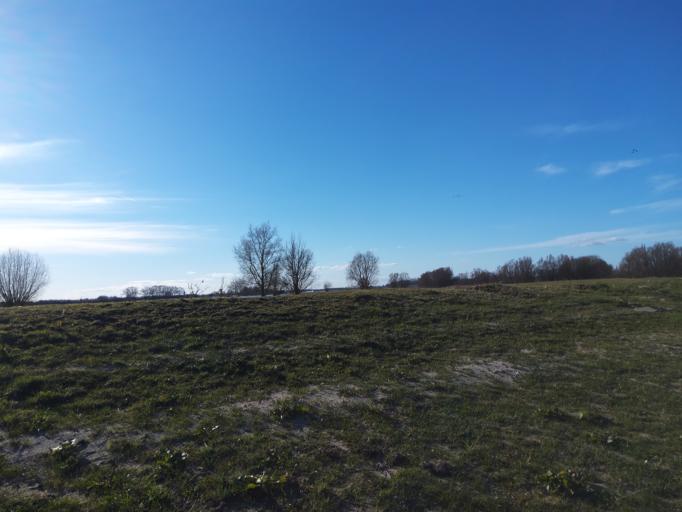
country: NL
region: Gelderland
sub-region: Gemeente Neerijnen
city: Neerijnen
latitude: 51.8228
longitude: 5.3260
